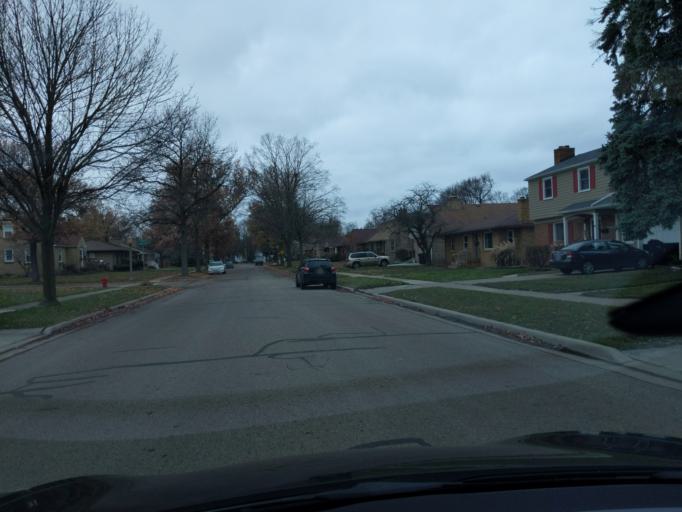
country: US
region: Michigan
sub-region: Ingham County
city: Lansing
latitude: 42.7088
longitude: -84.5784
